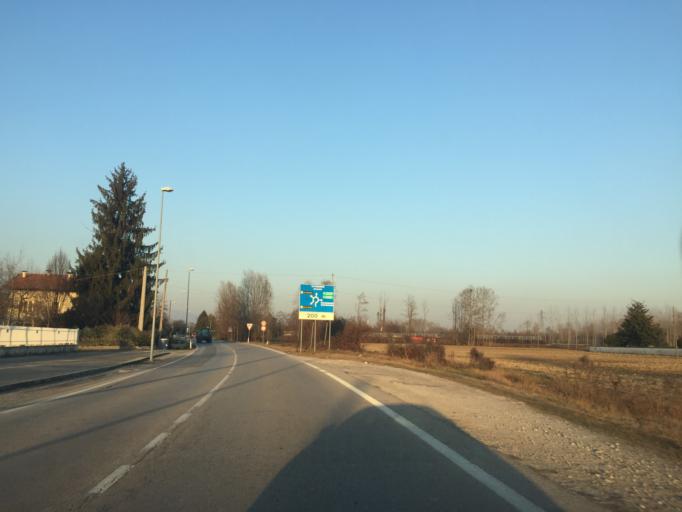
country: IT
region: Friuli Venezia Giulia
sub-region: Provincia di Pordenone
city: Vigonovo-Fontanafredda
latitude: 45.9761
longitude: 12.5281
